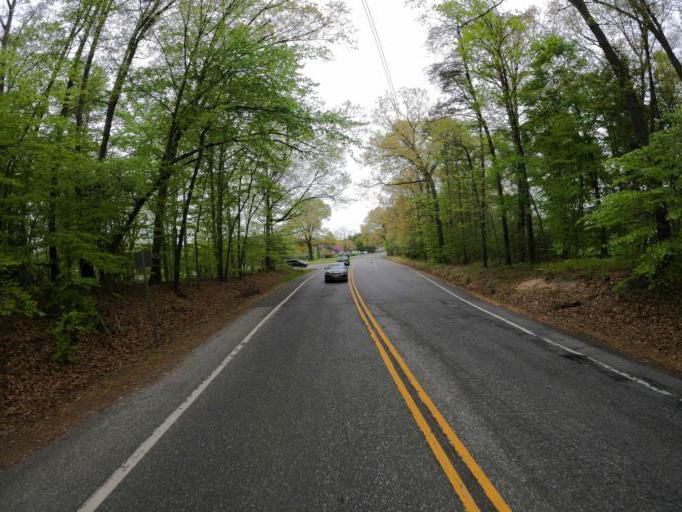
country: US
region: Maryland
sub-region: Anne Arundel County
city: Crofton
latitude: 38.9968
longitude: -76.7404
